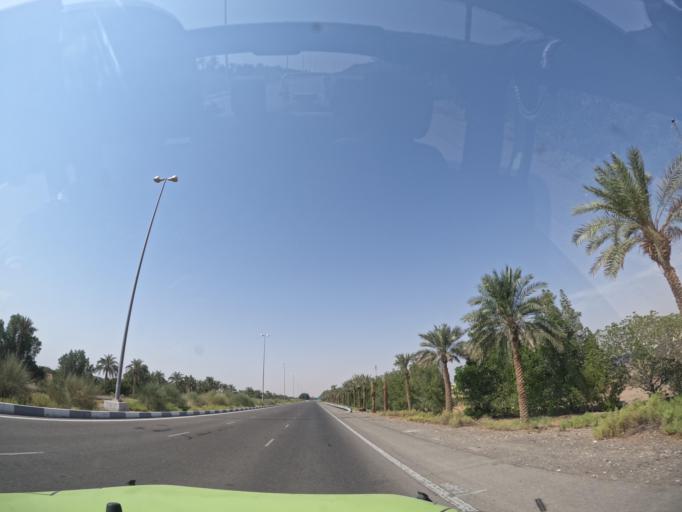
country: AE
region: Abu Dhabi
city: Al Ain
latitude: 24.2063
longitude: 55.5989
